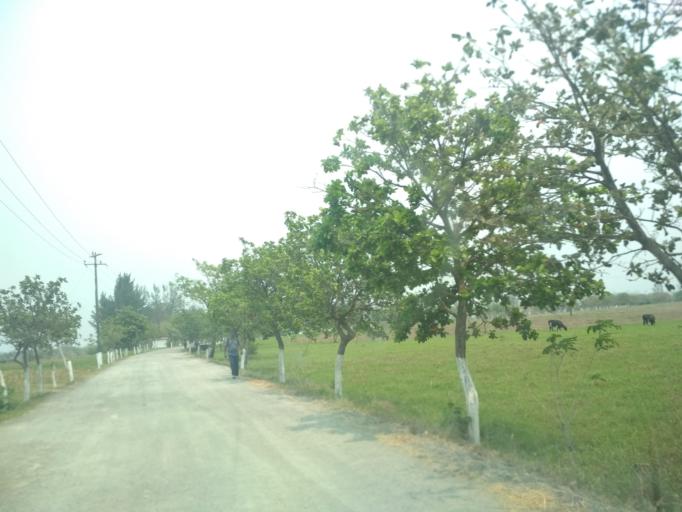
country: MX
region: Veracruz
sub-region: Veracruz
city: Las Amapolas
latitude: 19.1649
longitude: -96.2135
